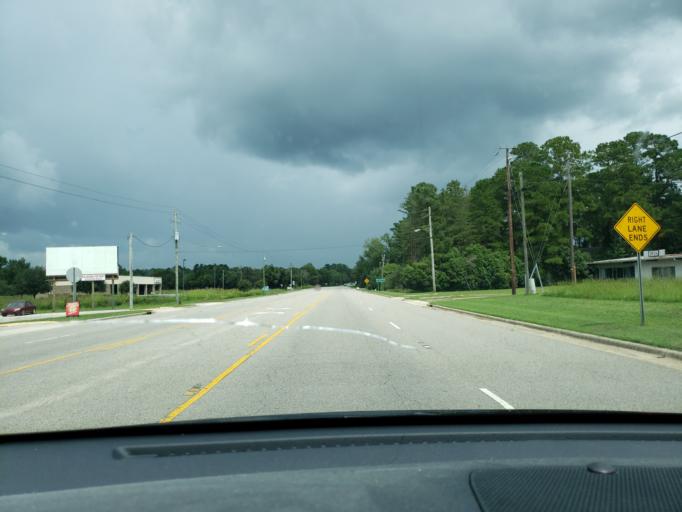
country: US
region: North Carolina
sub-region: Bladen County
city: Bladenboro
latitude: 34.4938
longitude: -78.6597
